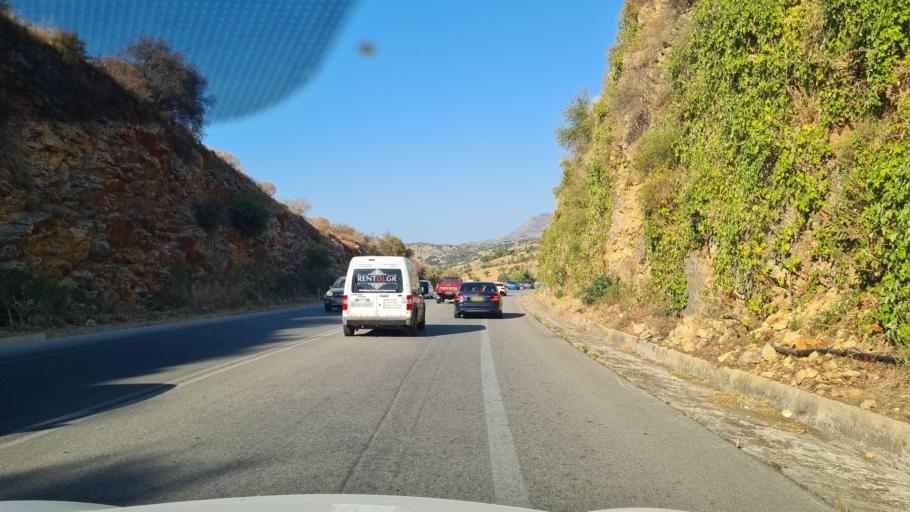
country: GR
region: Crete
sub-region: Nomos Chanias
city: Kalivai
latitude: 35.4169
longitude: 24.1486
